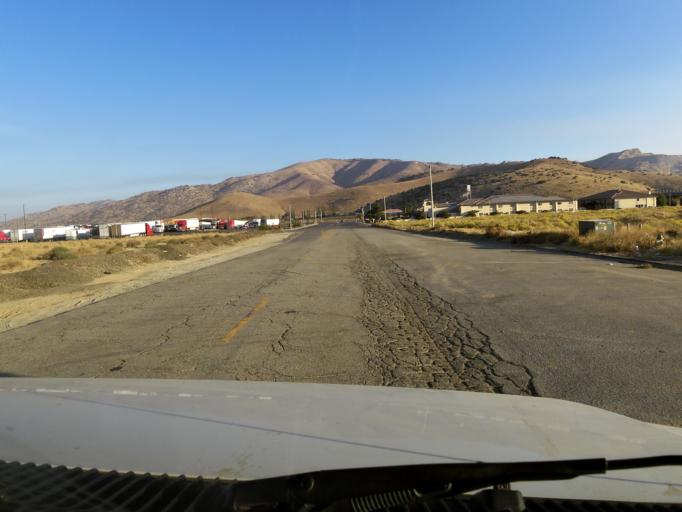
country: US
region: California
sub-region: Kern County
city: Tehachapi
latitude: 35.1243
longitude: -118.4143
